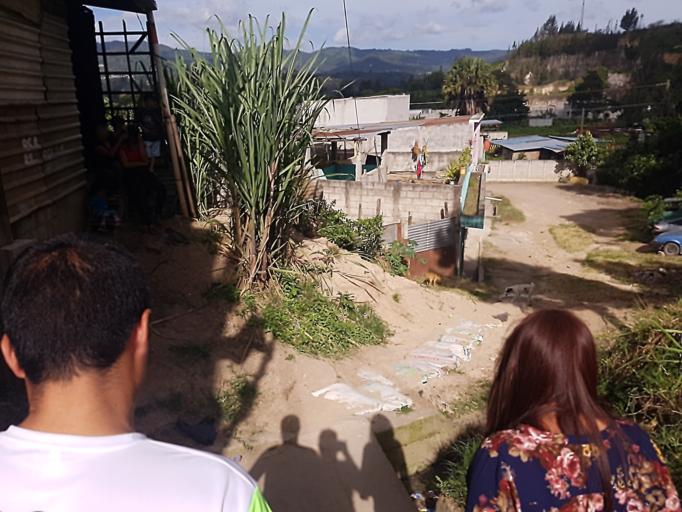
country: GT
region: Guatemala
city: Petapa
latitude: 14.5025
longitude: -90.5548
